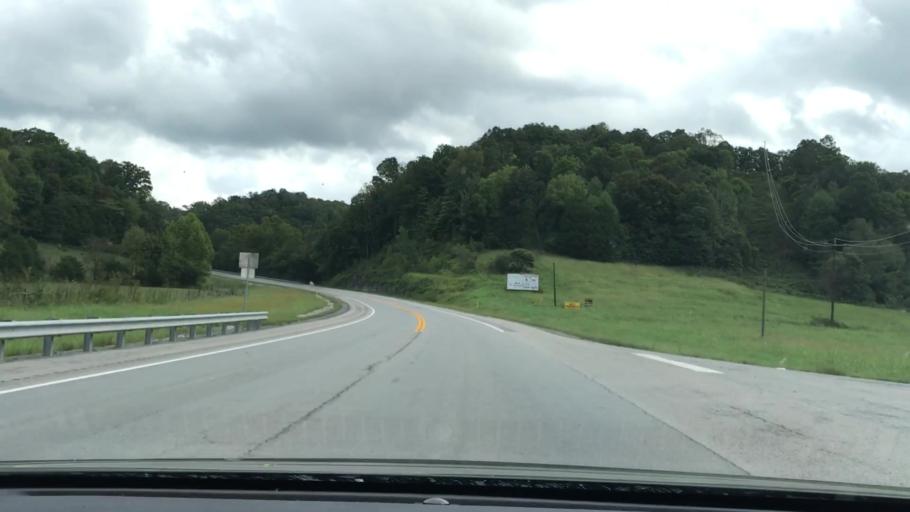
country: US
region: Kentucky
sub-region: Cumberland County
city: Burkesville
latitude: 36.7953
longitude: -85.3908
